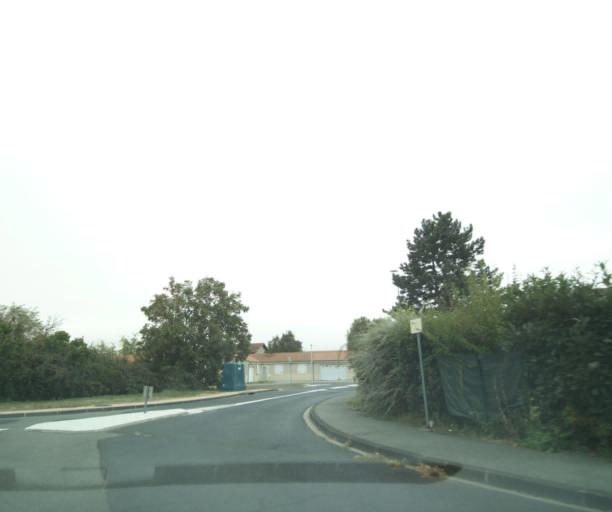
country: FR
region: Auvergne
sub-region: Departement du Puy-de-Dome
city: Gerzat
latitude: 45.8376
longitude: 3.1499
